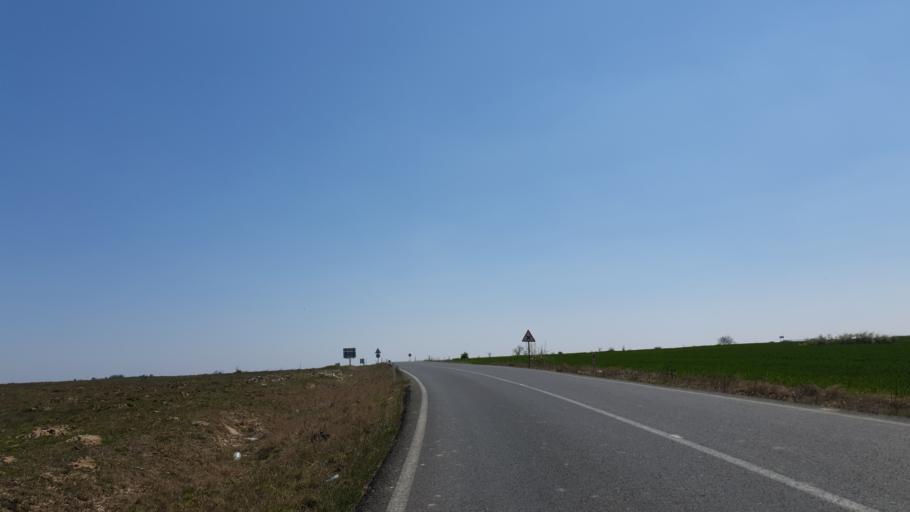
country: TR
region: Tekirdag
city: Velimese
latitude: 41.3273
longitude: 27.9219
